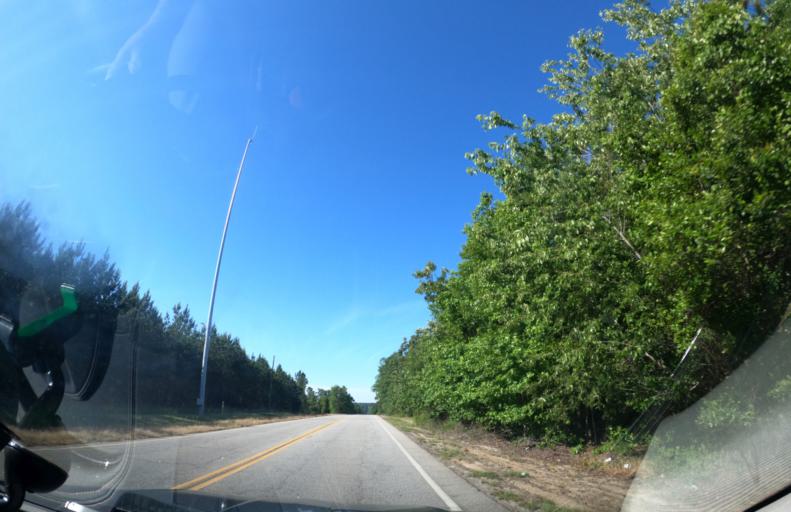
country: US
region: Georgia
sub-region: Columbia County
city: Harlem
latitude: 33.3901
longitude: -82.3154
